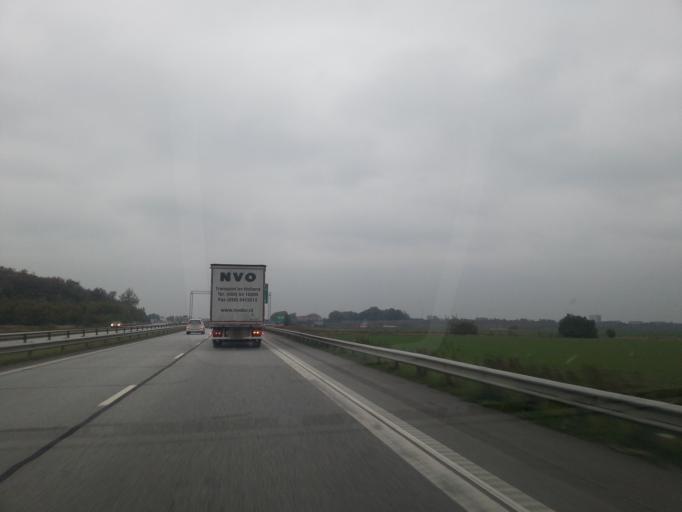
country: SE
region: Skane
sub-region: Malmo
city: Tygelsjo
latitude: 55.5415
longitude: 13.0053
